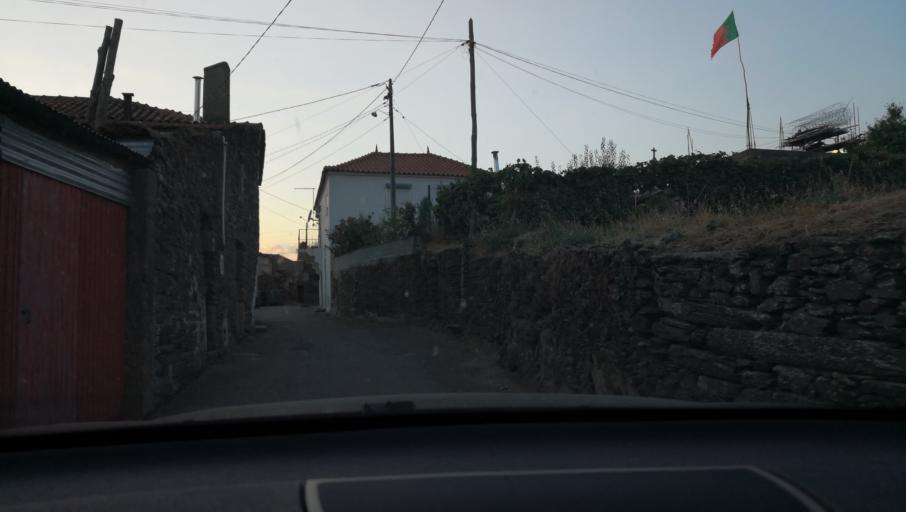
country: PT
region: Vila Real
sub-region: Sabrosa
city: Vilela
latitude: 41.2234
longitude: -7.6026
